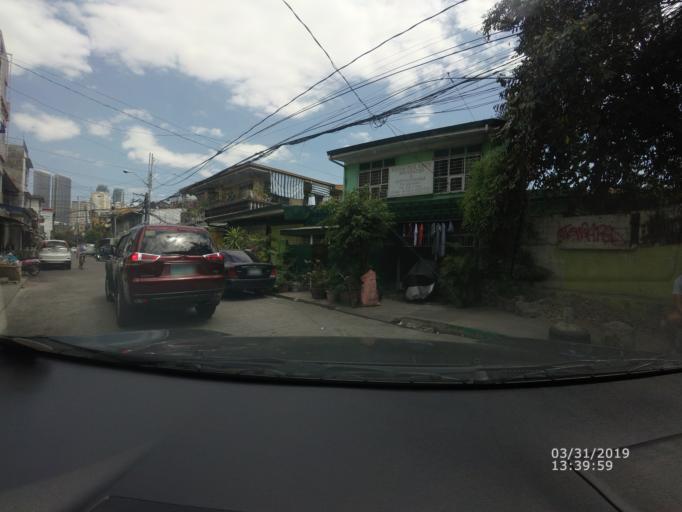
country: PH
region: Metro Manila
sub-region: Mandaluyong
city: Mandaluyong City
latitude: 14.5822
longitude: 121.0453
